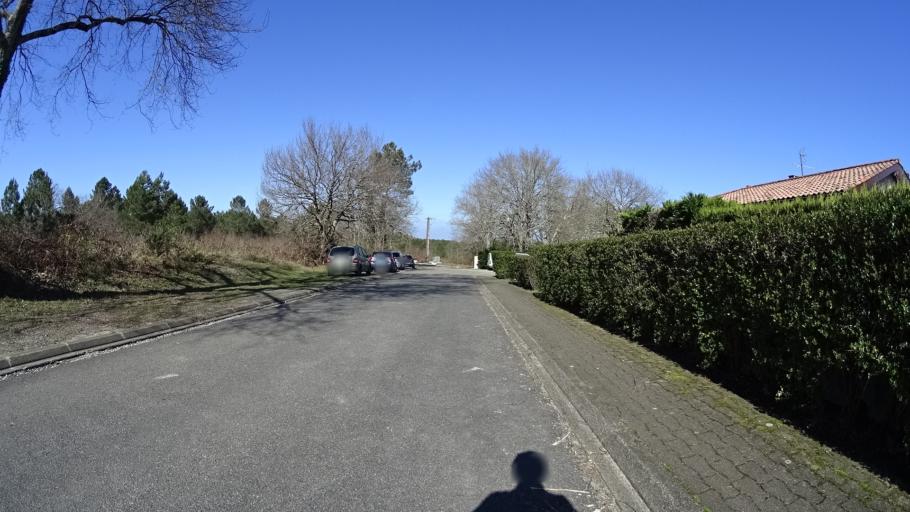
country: FR
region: Aquitaine
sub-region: Departement des Landes
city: Saint-Paul-les-Dax
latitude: 43.7344
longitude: -1.0840
